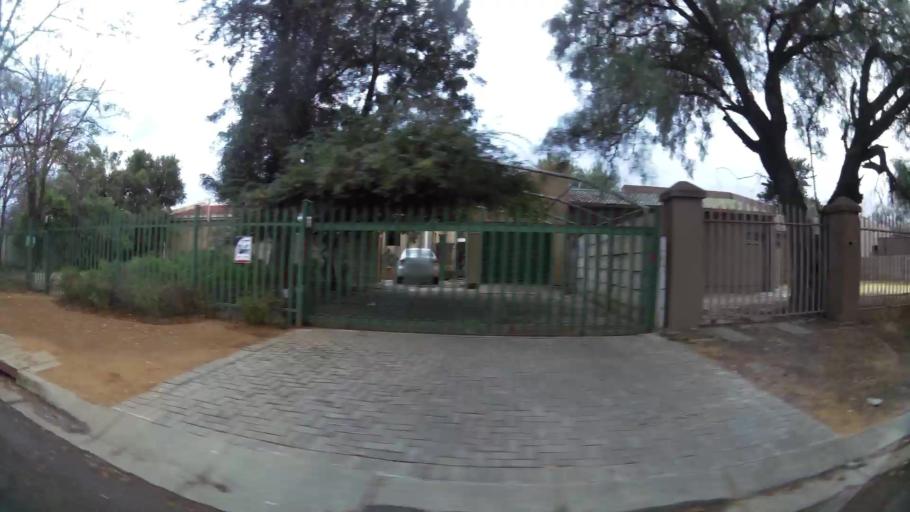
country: ZA
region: Orange Free State
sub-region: Lejweleputswa District Municipality
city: Welkom
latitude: -27.9511
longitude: 26.7323
